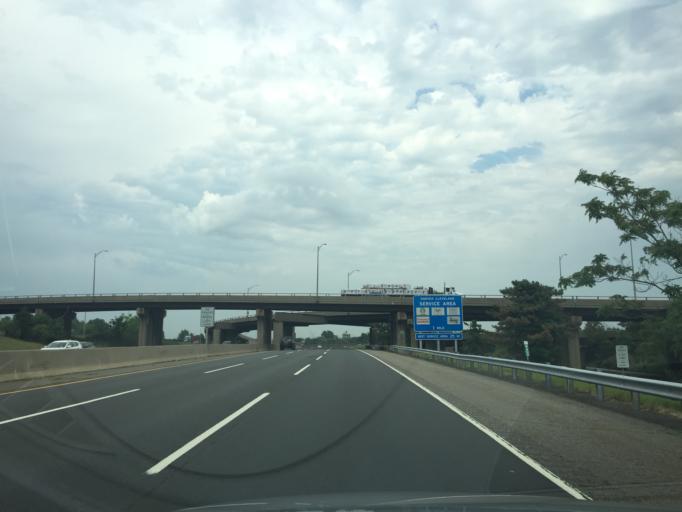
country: US
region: New Jersey
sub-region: Middlesex County
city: Woodbridge
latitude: 40.5441
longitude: -74.2891
